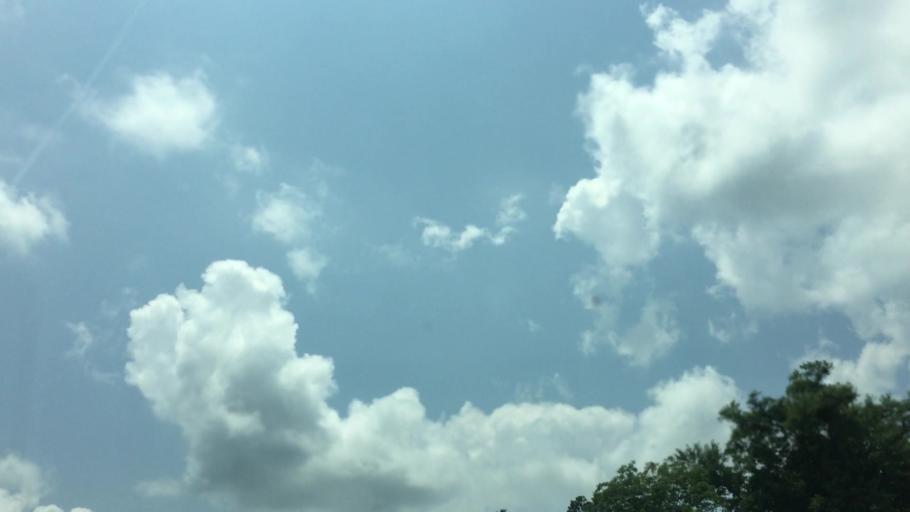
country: US
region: Georgia
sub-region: Carroll County
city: Villa Rica
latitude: 33.6108
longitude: -84.8952
